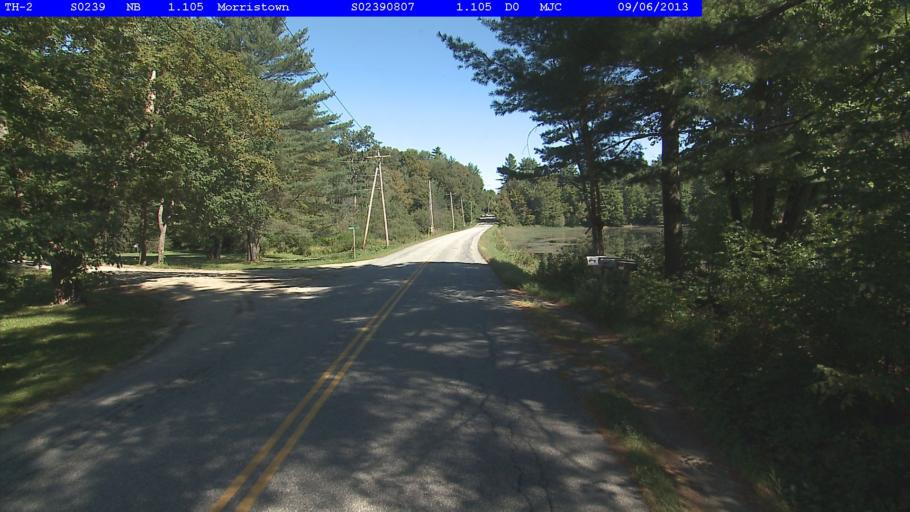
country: US
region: Vermont
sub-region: Lamoille County
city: Morristown
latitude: 44.5699
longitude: -72.6143
